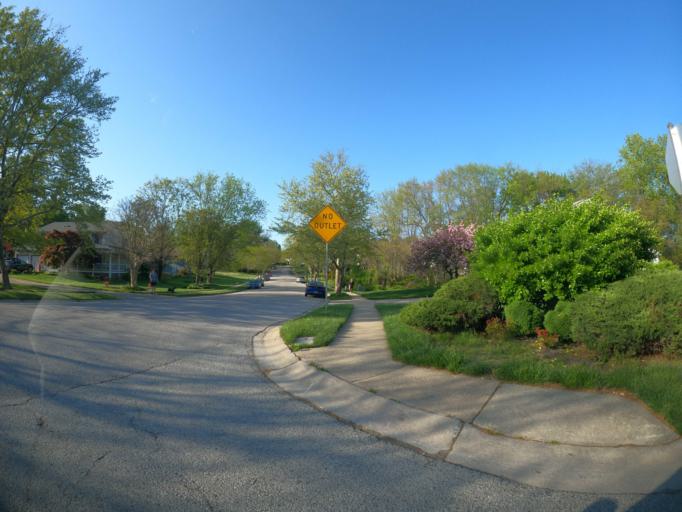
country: US
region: Maryland
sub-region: Howard County
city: Columbia
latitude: 39.2124
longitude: -76.8104
